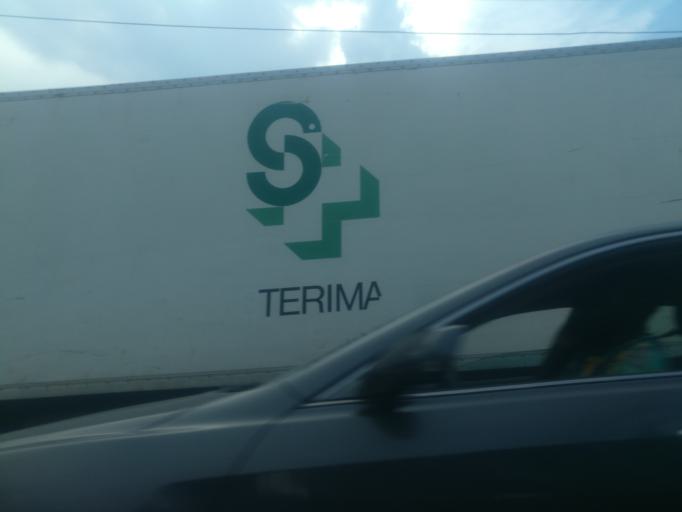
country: NG
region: Oyo
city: Ibadan
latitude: 7.3650
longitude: 3.8528
